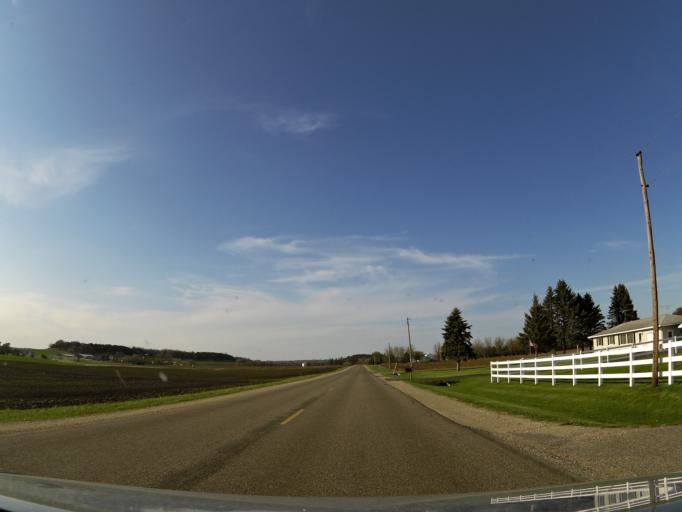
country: US
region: Wisconsin
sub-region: Pierce County
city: River Falls
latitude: 44.8109
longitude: -92.6448
